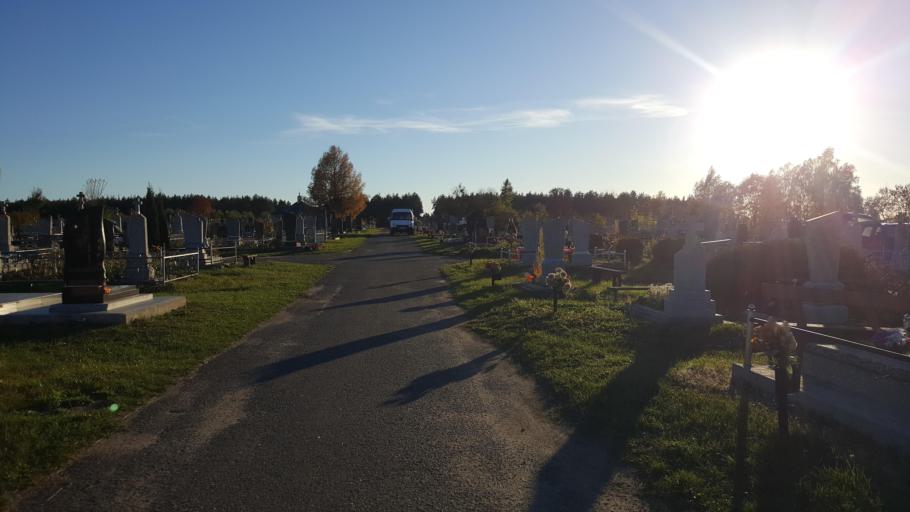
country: BY
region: Brest
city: Kamyanyets
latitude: 52.3958
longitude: 23.8406
